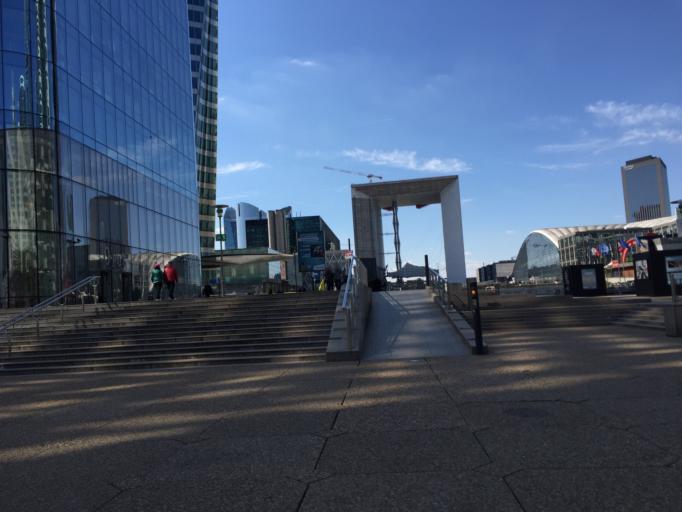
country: FR
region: Ile-de-France
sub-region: Departement des Hauts-de-Seine
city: La Defense
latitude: 48.8898
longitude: 2.2434
